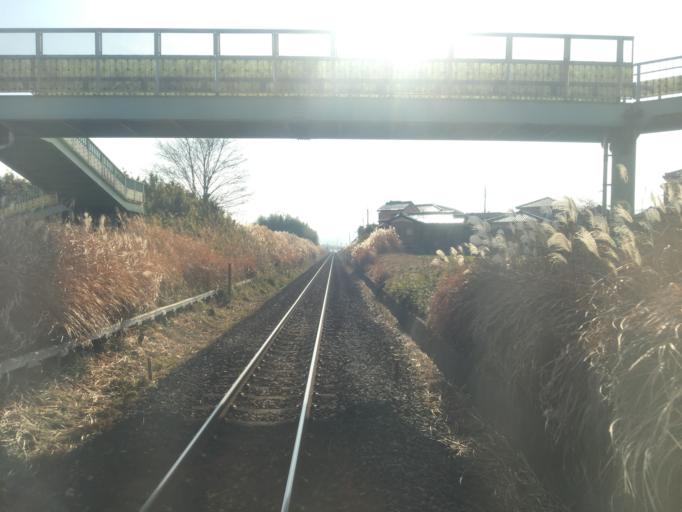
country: JP
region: Gunma
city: Fujioka
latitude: 36.2337
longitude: 139.0825
